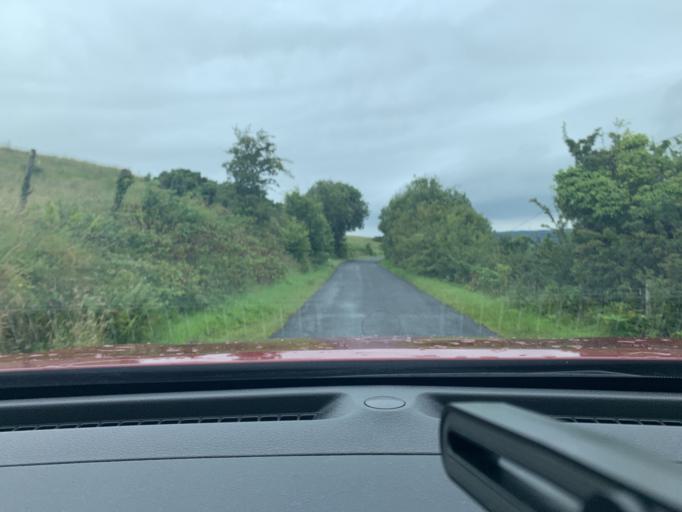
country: GB
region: Northern Ireland
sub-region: Fermanagh District
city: Enniskillen
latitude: 54.2733
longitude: -7.8557
